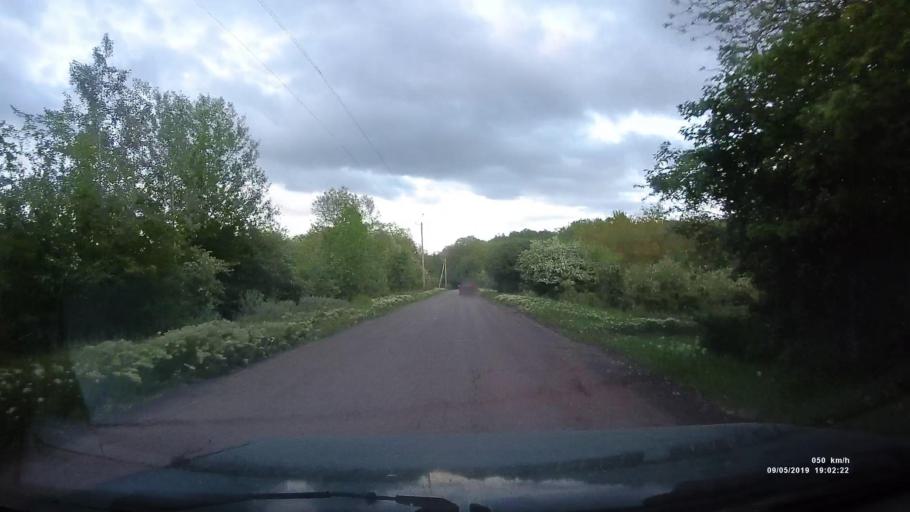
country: RU
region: Krasnodarskiy
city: Kanelovskaya
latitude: 46.7452
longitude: 39.1523
